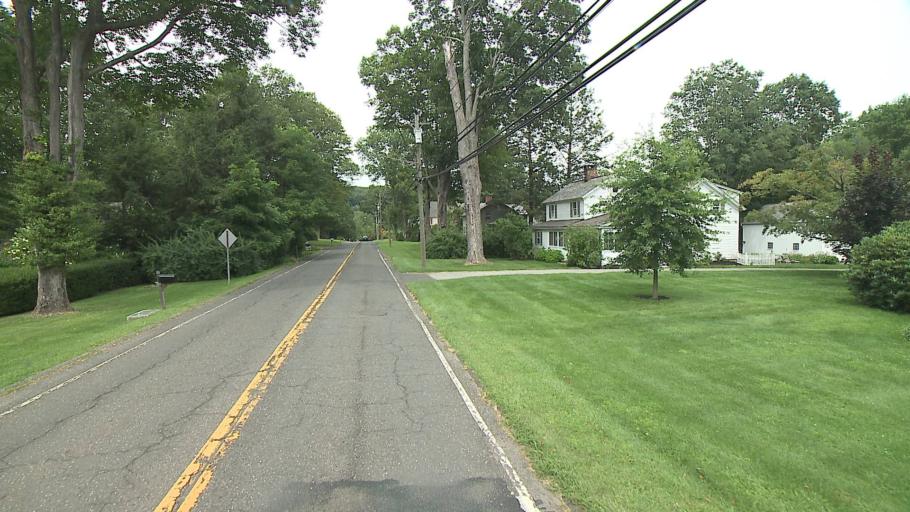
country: US
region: Connecticut
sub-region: Litchfield County
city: New Milford
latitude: 41.5365
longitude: -73.3669
